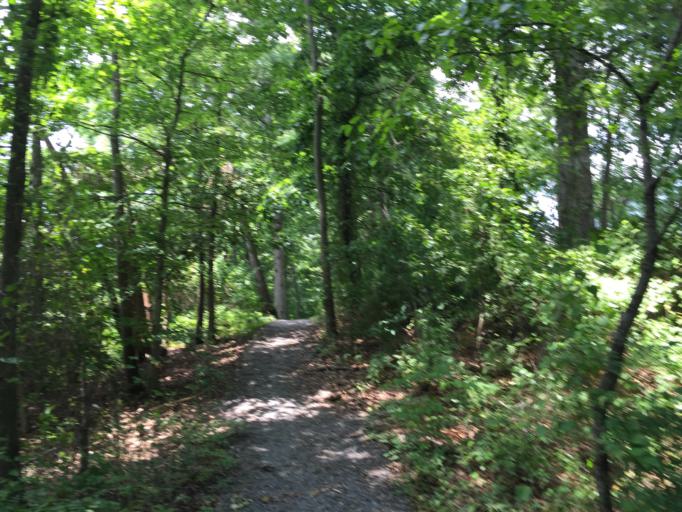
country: US
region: Maryland
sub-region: Charles County
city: Indian Head
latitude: 38.5904
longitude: -77.1584
